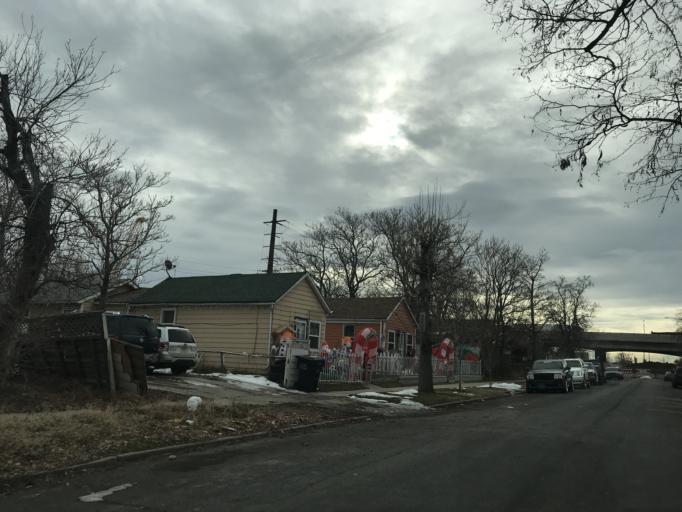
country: US
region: Colorado
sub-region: Adams County
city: Commerce City
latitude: 39.7819
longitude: -104.9645
